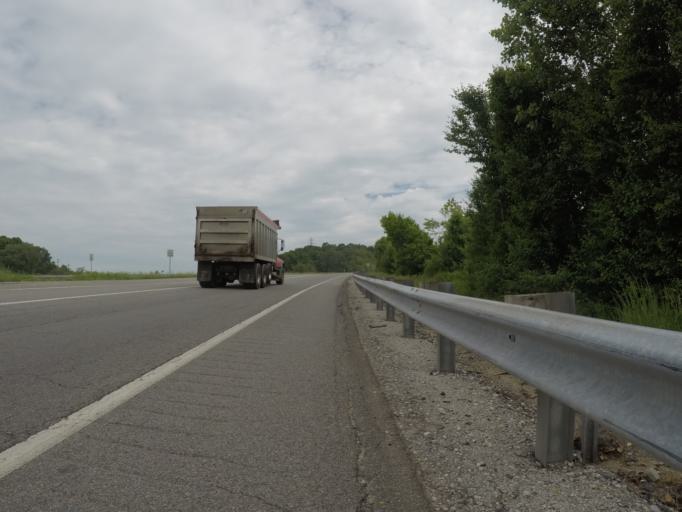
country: US
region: West Virginia
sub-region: Wayne County
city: Kenova
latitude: 38.3744
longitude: -82.5876
